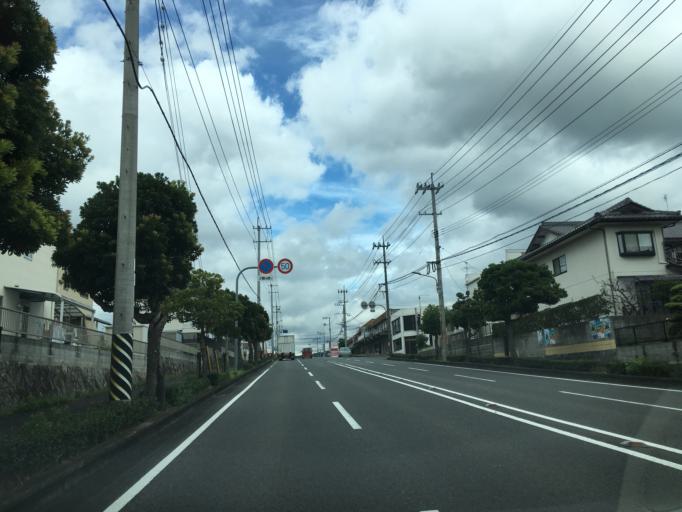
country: JP
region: Okayama
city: Okayama-shi
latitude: 34.7793
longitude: 134.0381
